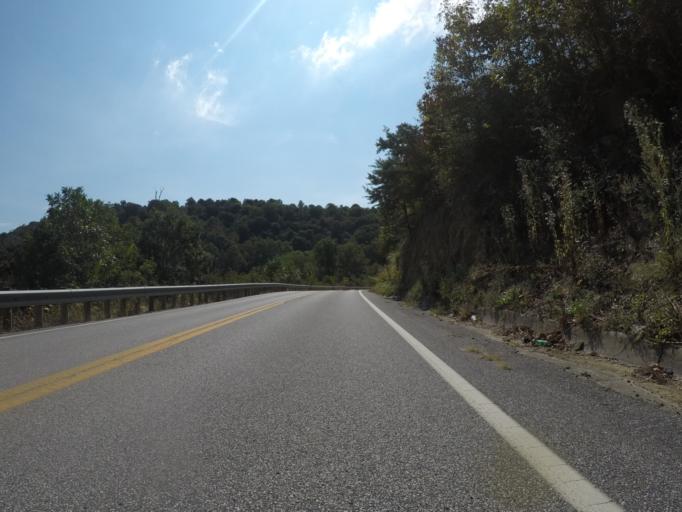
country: US
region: West Virginia
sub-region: Cabell County
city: Lesage
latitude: 38.5417
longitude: -82.3913
